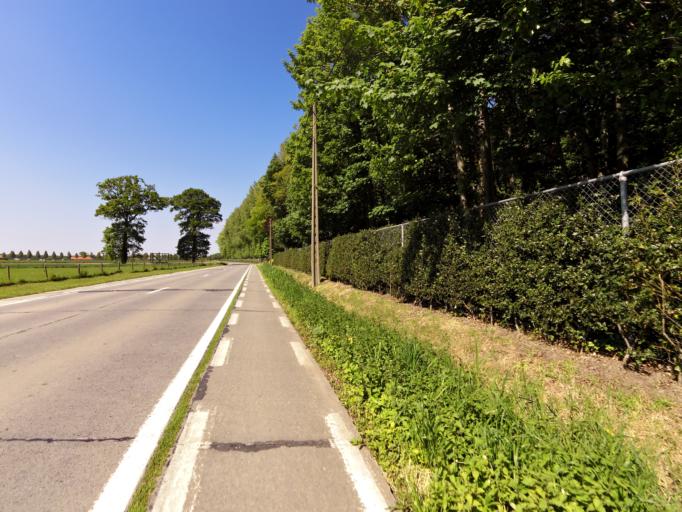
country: BE
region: Flanders
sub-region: Provincie West-Vlaanderen
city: Koekelare
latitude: 51.0594
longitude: 2.9391
